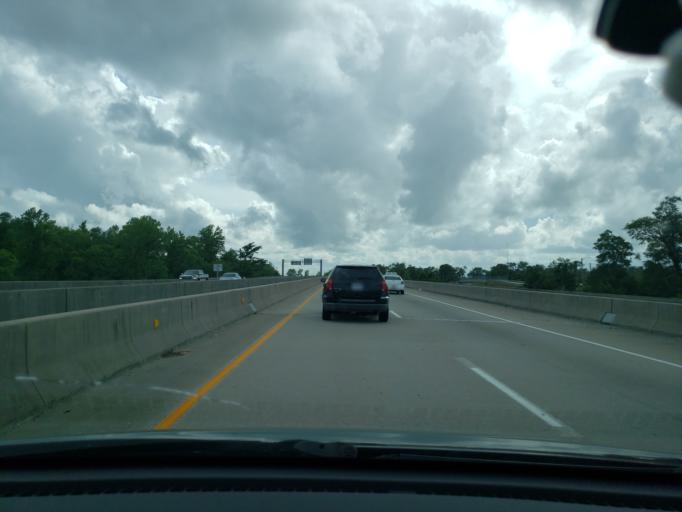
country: US
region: North Carolina
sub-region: New Hanover County
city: Wilmington
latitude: 34.2559
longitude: -77.9398
